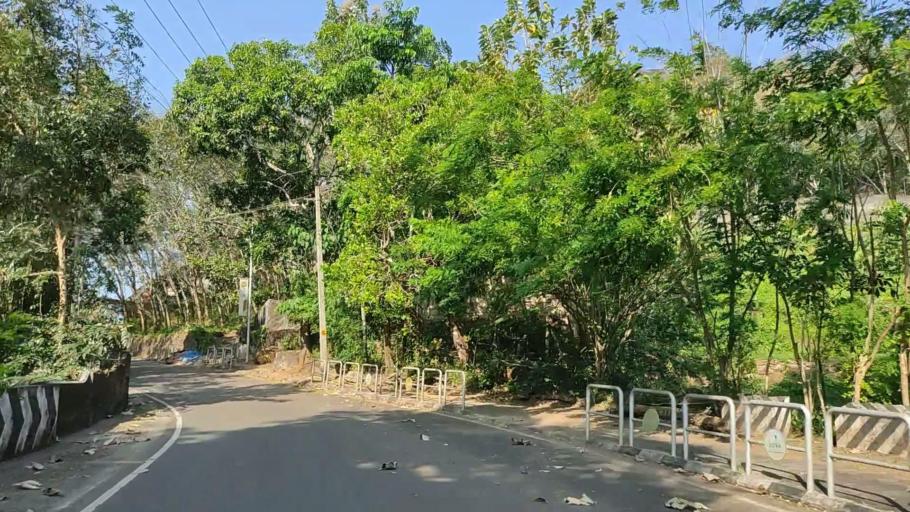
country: IN
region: Kerala
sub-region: Kollam
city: Punalur
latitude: 8.8610
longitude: 76.8684
